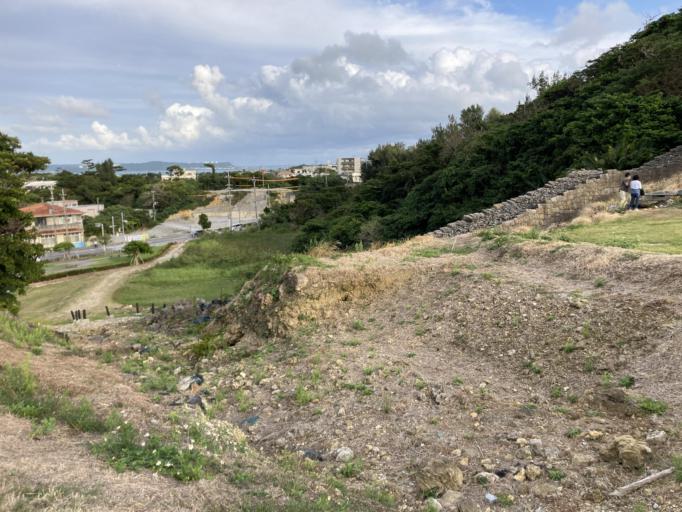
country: JP
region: Okinawa
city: Katsuren-haebaru
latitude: 26.3304
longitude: 127.8798
